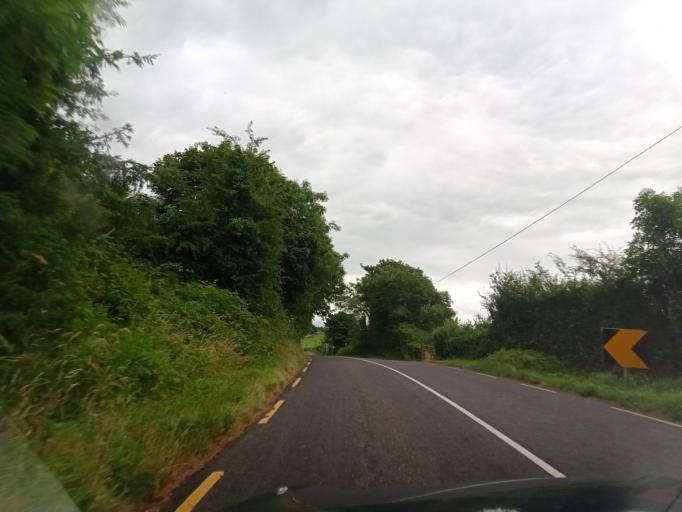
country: IE
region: Leinster
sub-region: Laois
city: Stradbally
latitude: 52.9228
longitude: -7.1931
